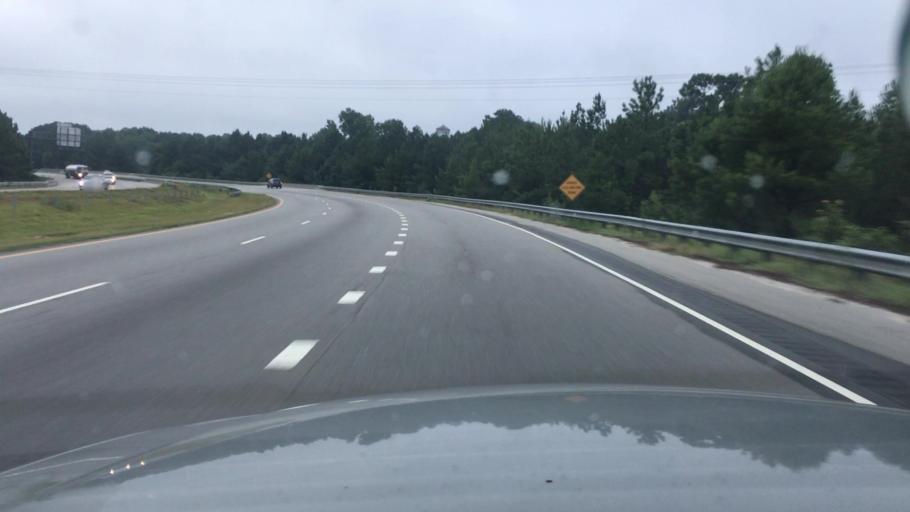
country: US
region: North Carolina
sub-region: Cumberland County
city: Fayetteville
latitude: 35.0406
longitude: -78.8918
